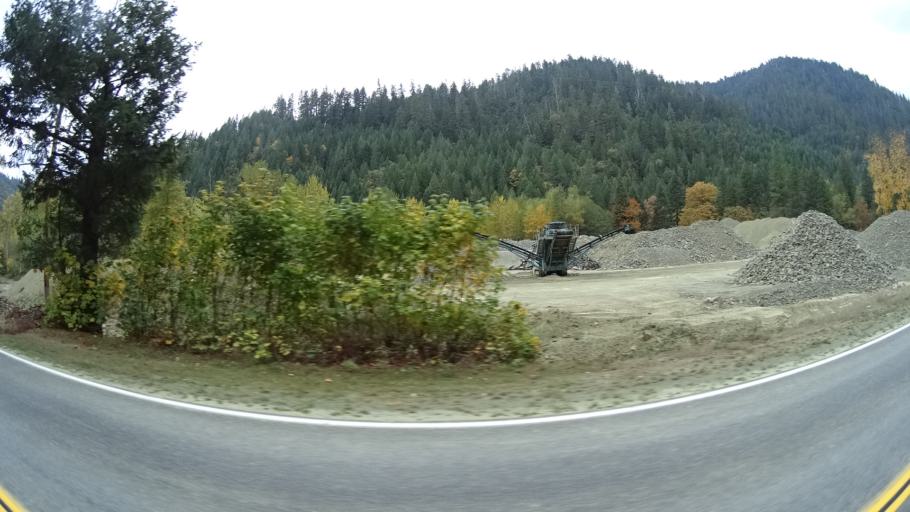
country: US
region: California
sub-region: Siskiyou County
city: Happy Camp
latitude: 41.8850
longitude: -123.4318
